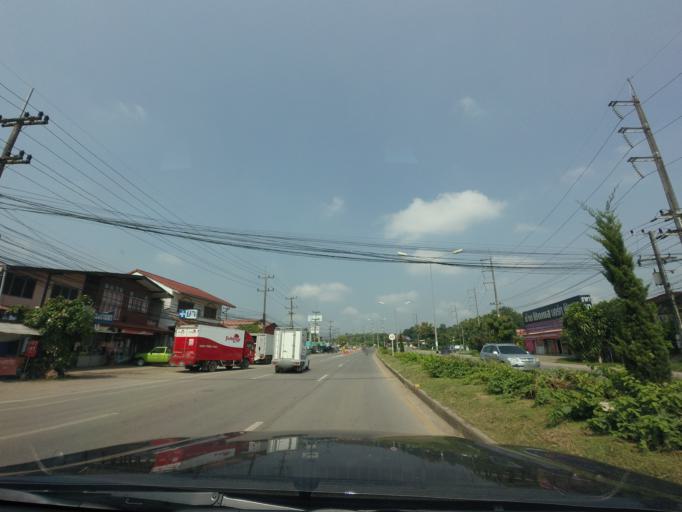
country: TH
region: Nan
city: Nan
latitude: 18.7847
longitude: 100.7453
